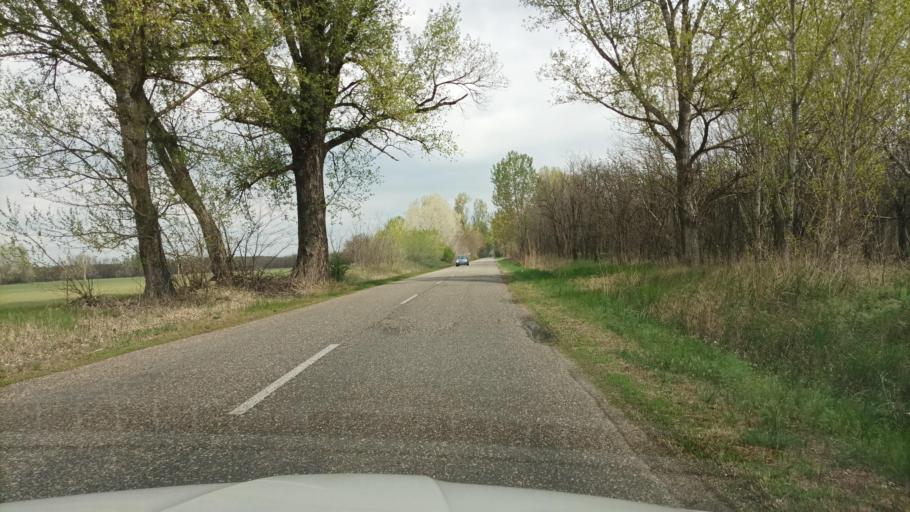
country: HU
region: Pest
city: Kocser
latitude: 47.0652
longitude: 19.8624
